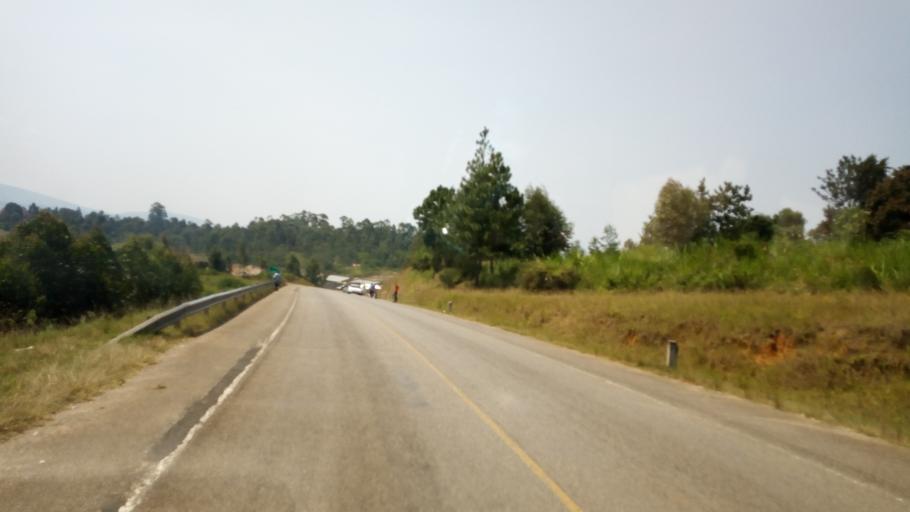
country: UG
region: Western Region
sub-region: Ntungamo District
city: Ntungamo
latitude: -0.8177
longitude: 30.1573
